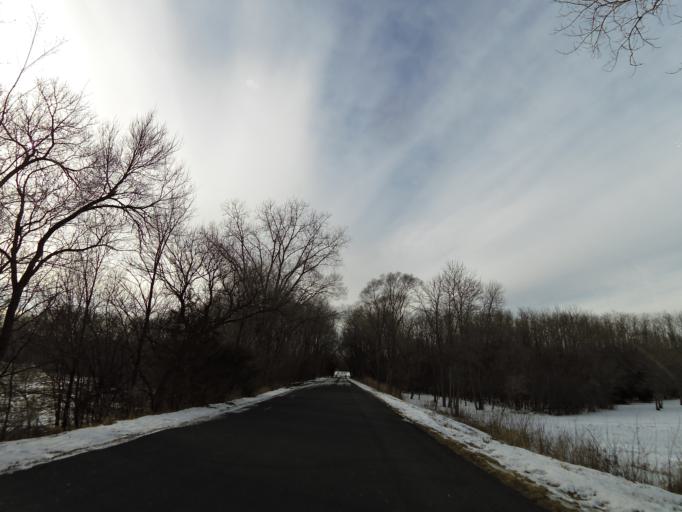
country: US
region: Minnesota
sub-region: Washington County
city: Lake Saint Croix Beach
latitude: 44.9157
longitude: -92.7674
